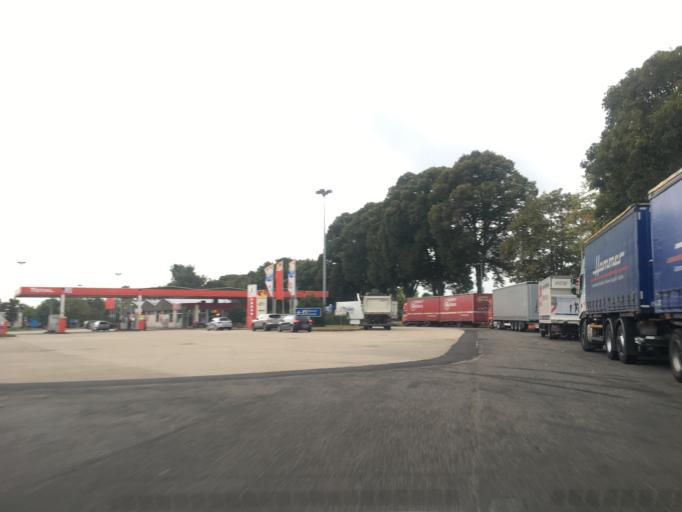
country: DE
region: North Rhine-Westphalia
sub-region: Regierungsbezirk Dusseldorf
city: Neubrueck
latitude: 51.1308
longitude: 6.6052
